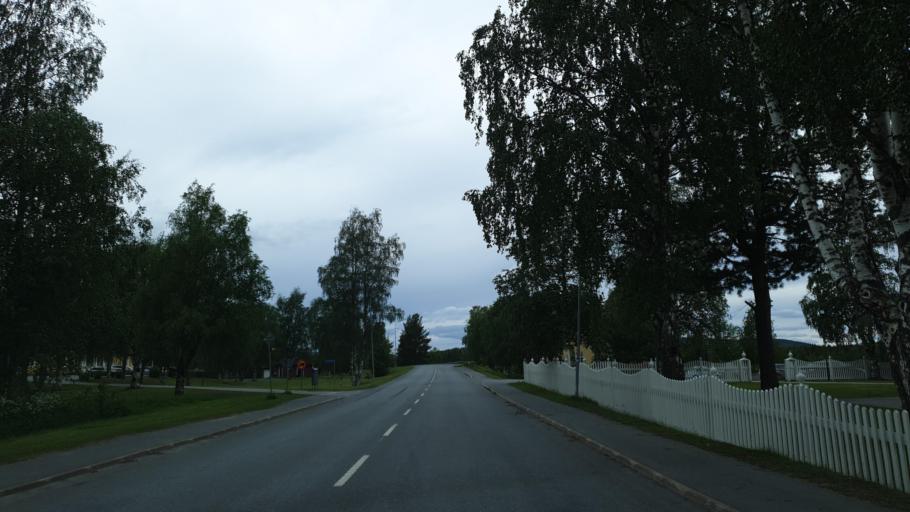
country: SE
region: Vaesterbotten
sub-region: Sorsele Kommun
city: Sorsele
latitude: 65.5415
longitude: 17.5153
